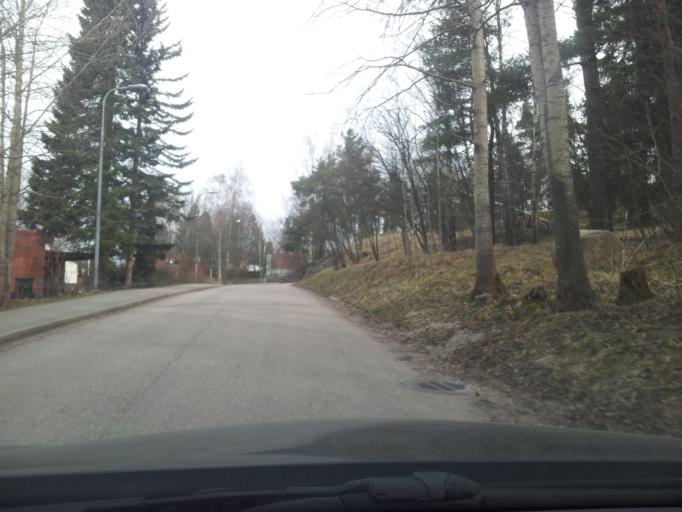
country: FI
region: Uusimaa
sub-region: Helsinki
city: Koukkuniemi
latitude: 60.1812
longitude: 24.7879
